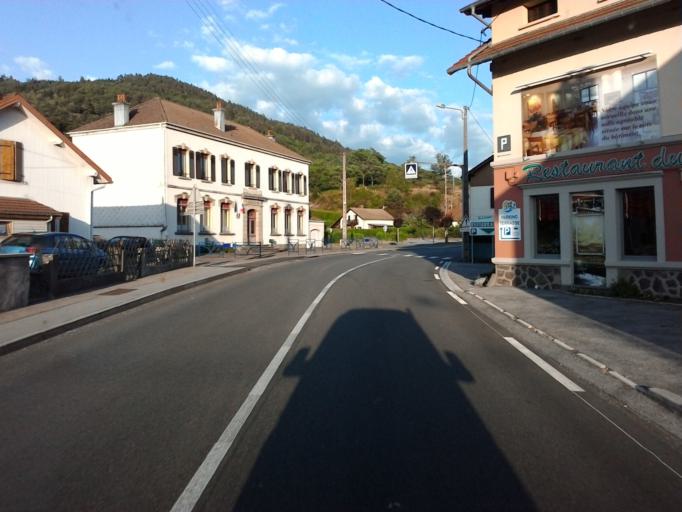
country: FR
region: Lorraine
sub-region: Departement des Vosges
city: Ramonchamp
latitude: 47.9065
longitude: 6.7099
